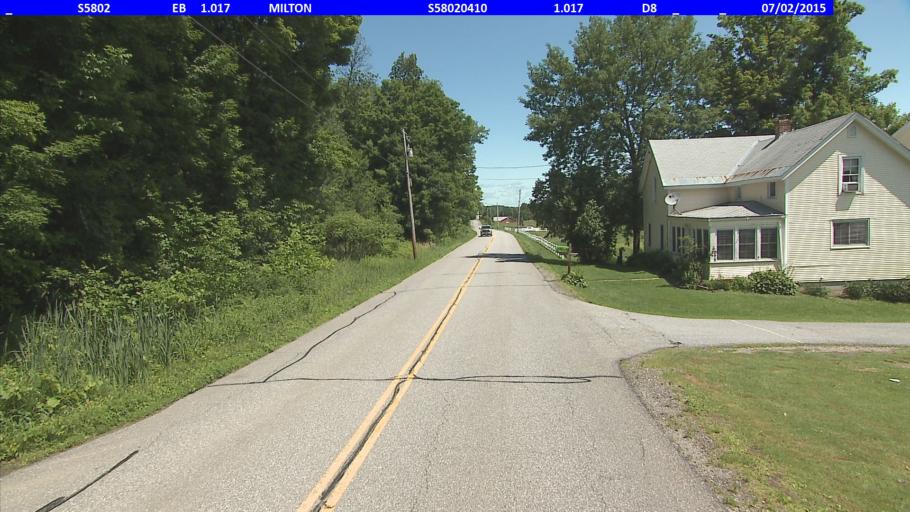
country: US
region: Vermont
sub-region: Chittenden County
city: Milton
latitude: 44.6218
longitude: -73.2000
